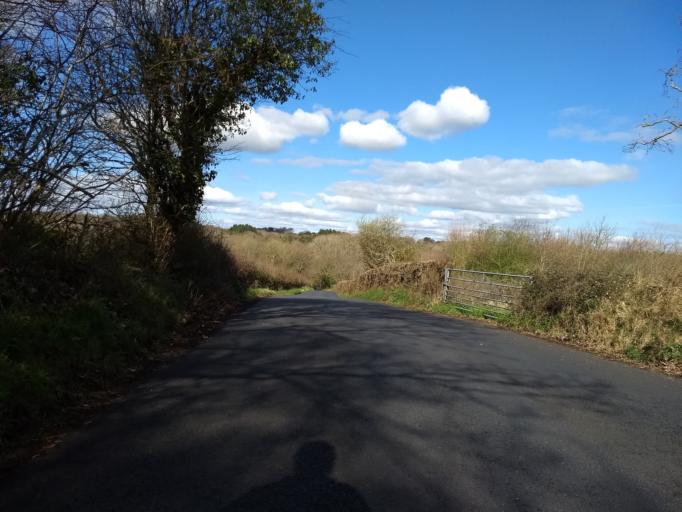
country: GB
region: England
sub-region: Isle of Wight
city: East Cowes
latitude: 50.7314
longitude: -1.2468
